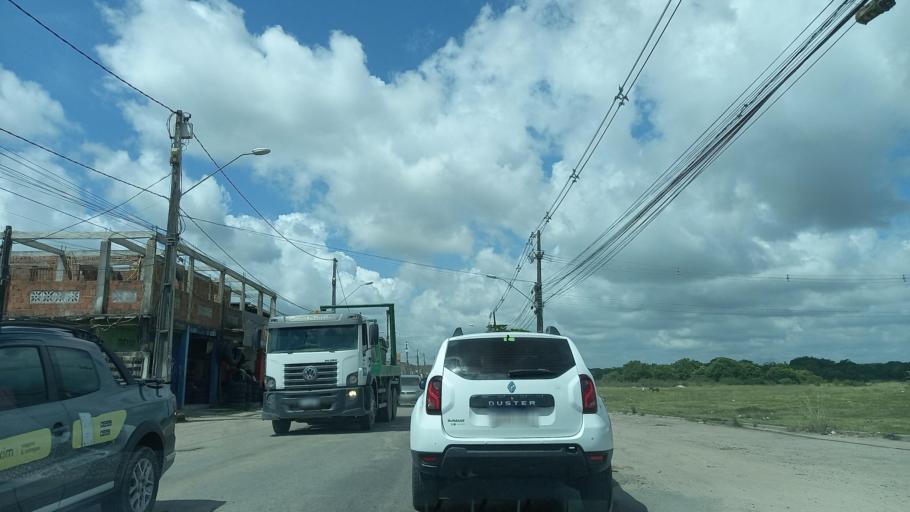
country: BR
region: Pernambuco
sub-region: Jaboatao Dos Guararapes
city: Jaboatao
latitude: -8.1566
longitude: -34.9676
